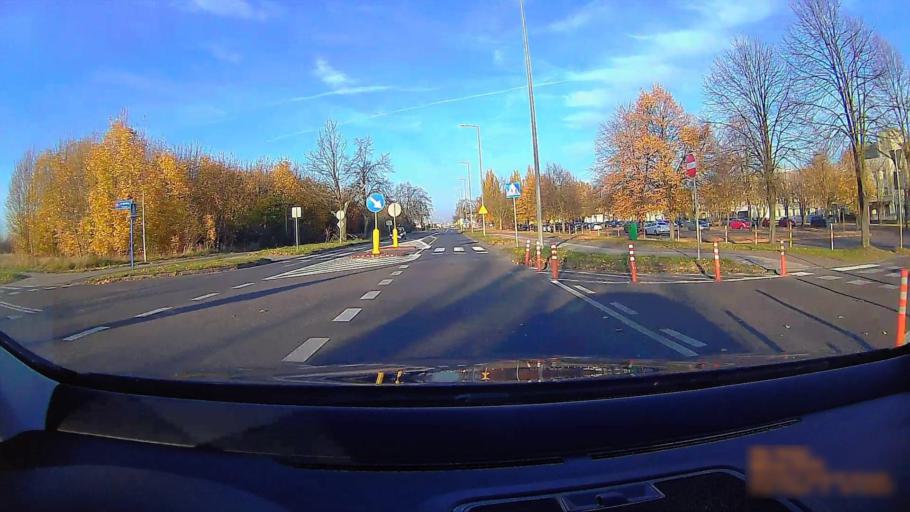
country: PL
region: Greater Poland Voivodeship
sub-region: Powiat koninski
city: Stare Miasto
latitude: 52.1948
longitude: 18.2373
